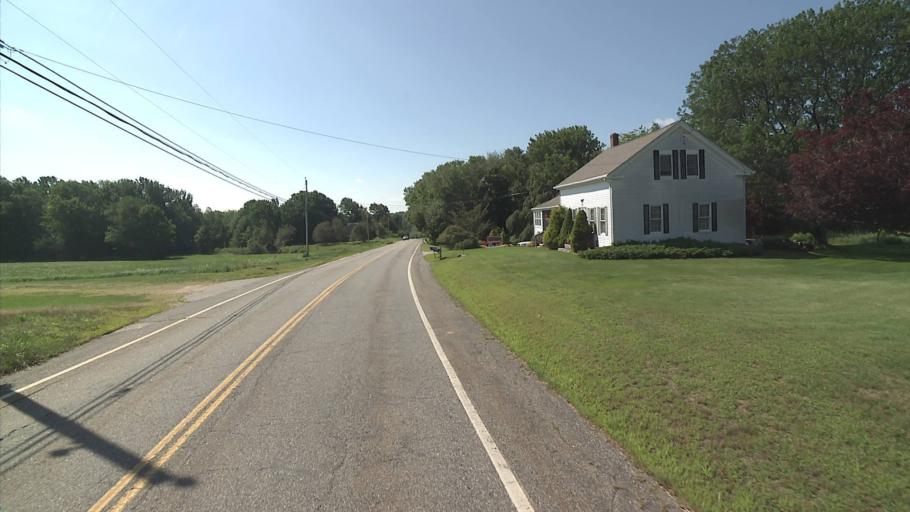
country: US
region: Connecticut
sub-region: Tolland County
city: Stafford Springs
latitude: 41.9229
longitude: -72.1920
